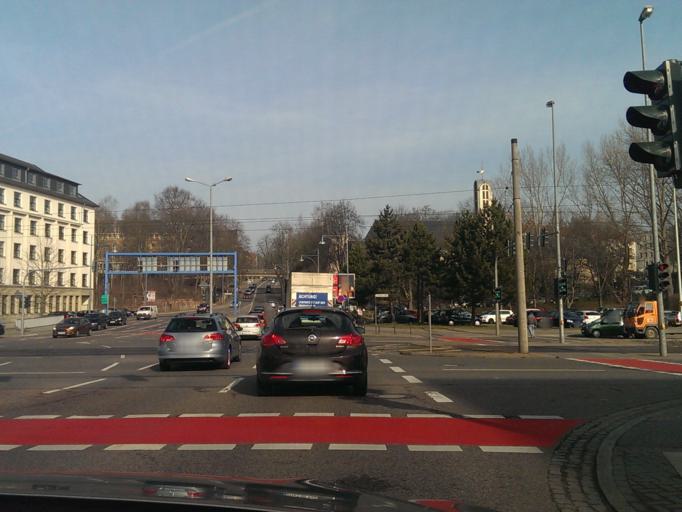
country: DE
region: Saxony
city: Chemnitz
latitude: 50.8275
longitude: 12.9130
